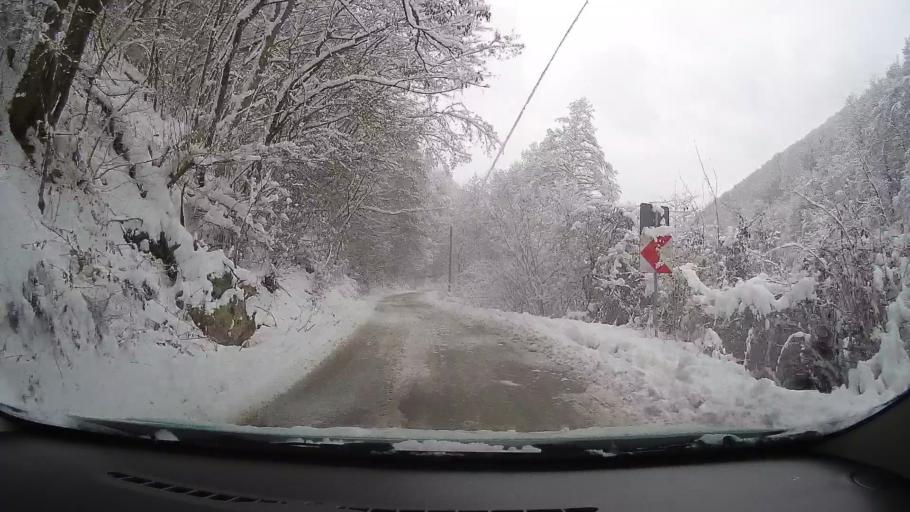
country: RO
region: Alba
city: Pianu de Sus
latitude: 45.8687
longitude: 23.4956
